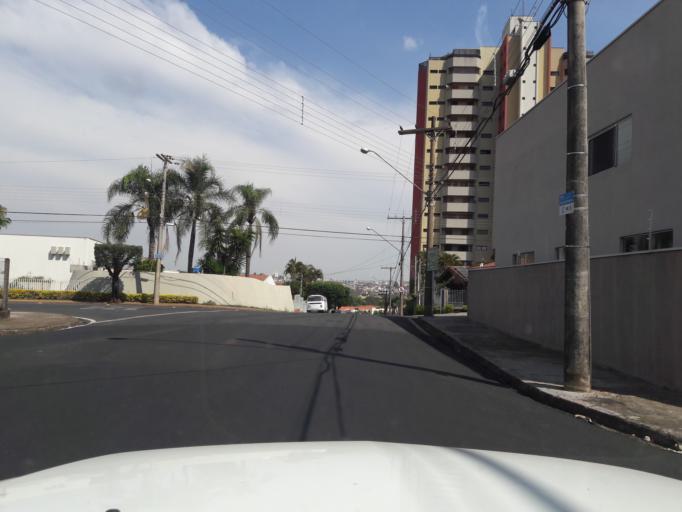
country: BR
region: Sao Paulo
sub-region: Moji-Guacu
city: Mogi-Gaucu
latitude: -22.3678
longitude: -46.9378
